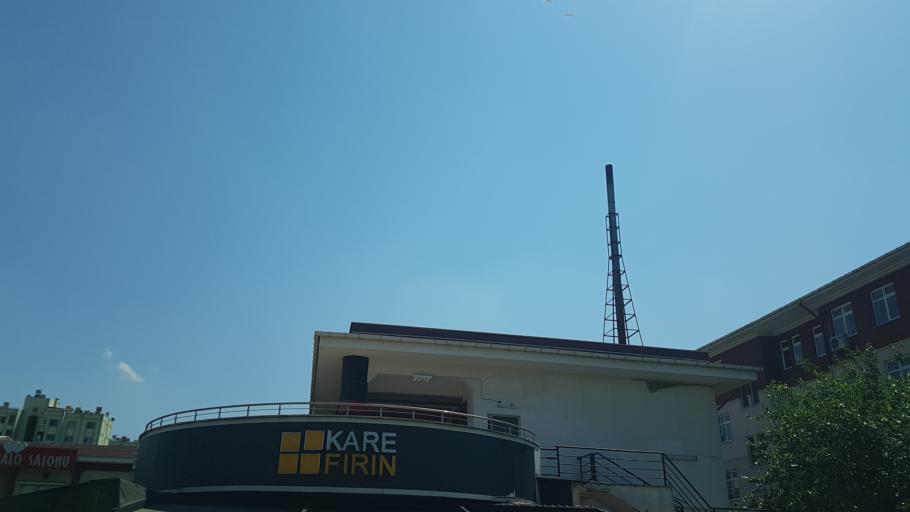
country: TR
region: Adana
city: Adana
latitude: 37.0296
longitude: 35.3566
